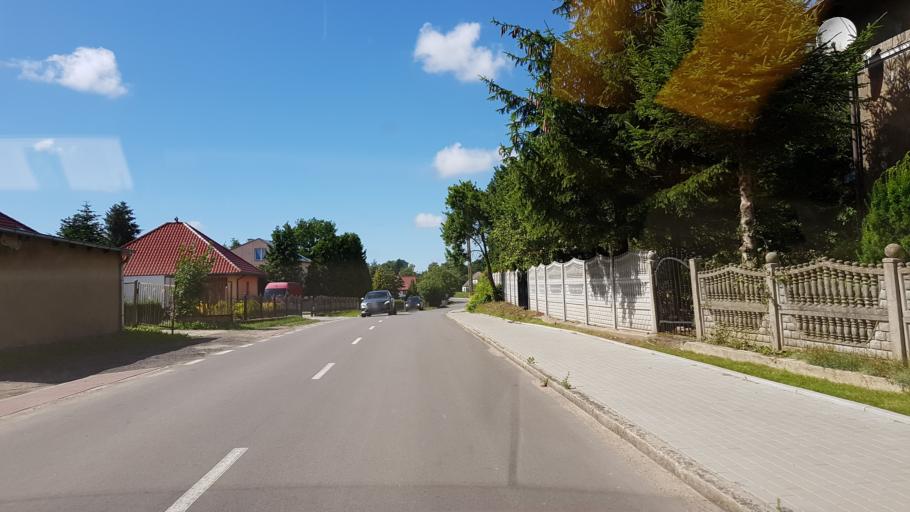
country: PL
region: West Pomeranian Voivodeship
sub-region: Powiat bialogardzki
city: Karlino
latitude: 54.1890
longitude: 15.9146
